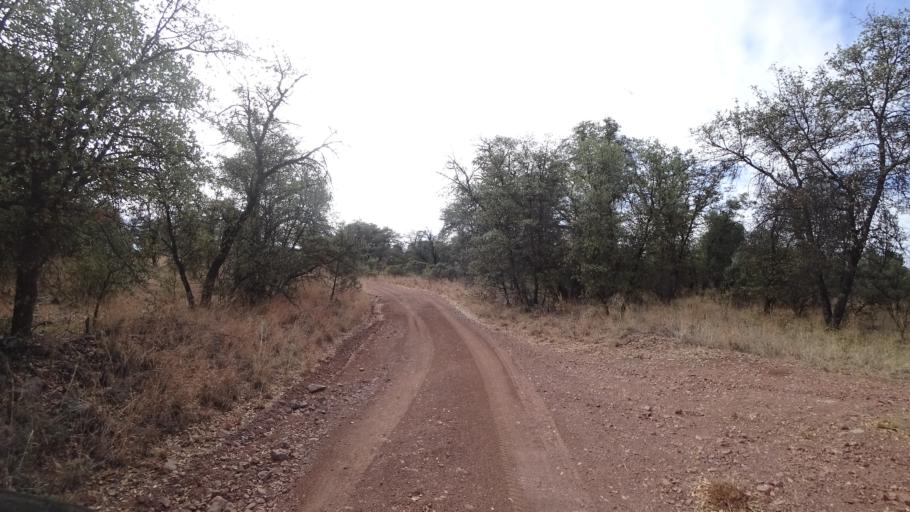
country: MX
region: Sonora
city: Santa Cruz
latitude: 31.4834
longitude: -110.5707
